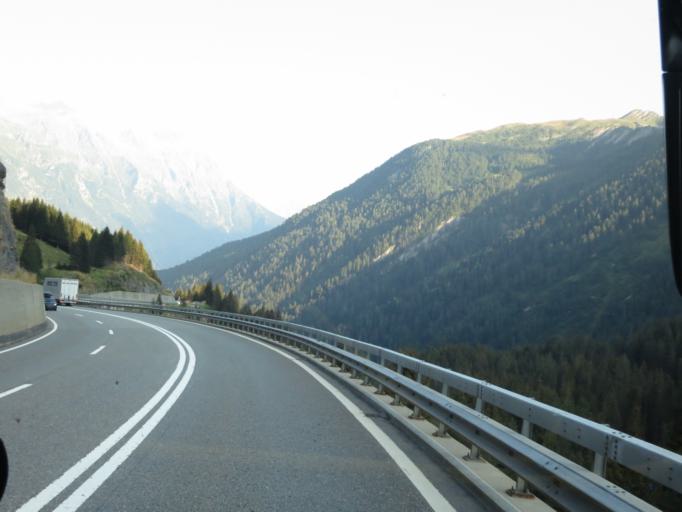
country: CH
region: Grisons
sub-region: Moesa District
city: Mesocco
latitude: 46.4377
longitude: 9.1933
